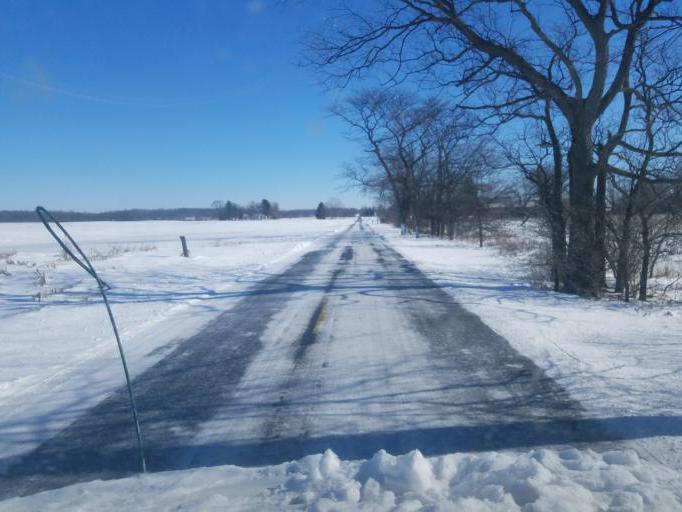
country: US
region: Ohio
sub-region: Delaware County
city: Delaware
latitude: 40.2874
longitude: -82.9951
